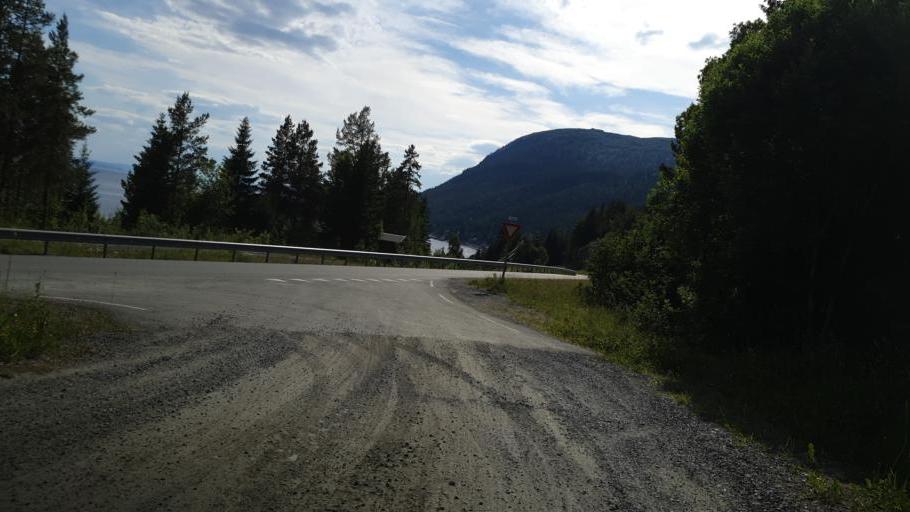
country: NO
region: Sor-Trondelag
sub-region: Trondheim
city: Trondheim
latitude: 63.5761
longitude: 10.3700
